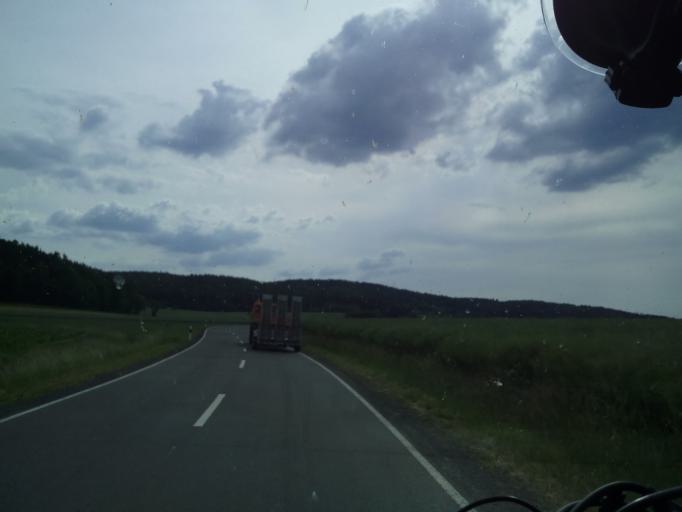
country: DE
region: Bavaria
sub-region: Regierungsbezirk Unterfranken
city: Pfarrweisach
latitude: 50.2026
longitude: 10.7161
